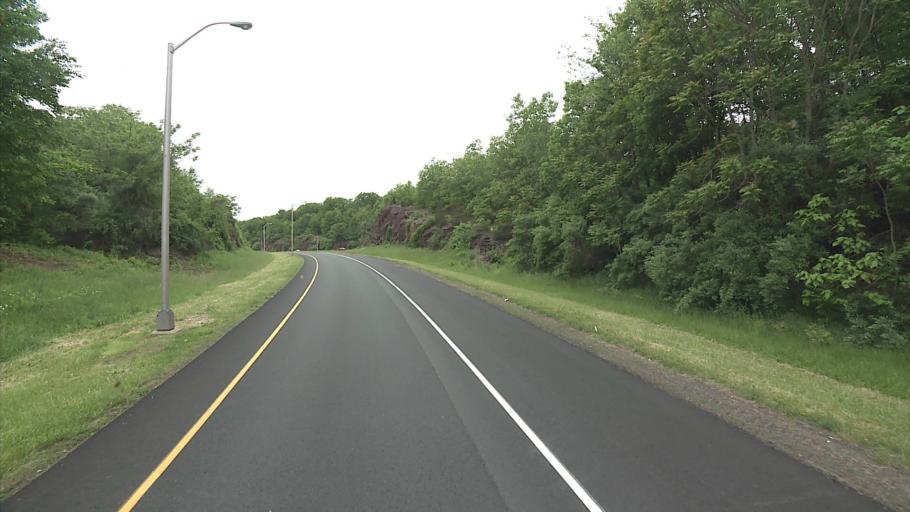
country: US
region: Connecticut
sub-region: Middlesex County
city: Cromwell
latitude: 41.6254
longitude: -72.6955
